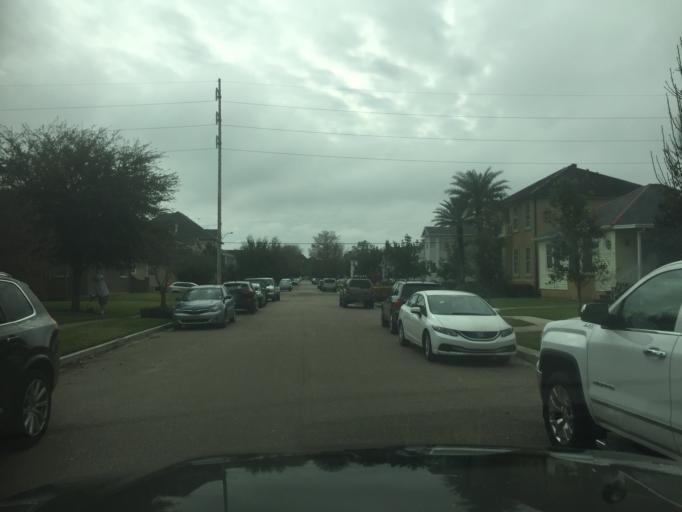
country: US
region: Louisiana
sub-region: Jefferson Parish
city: Metairie
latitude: 30.0015
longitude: -90.1072
